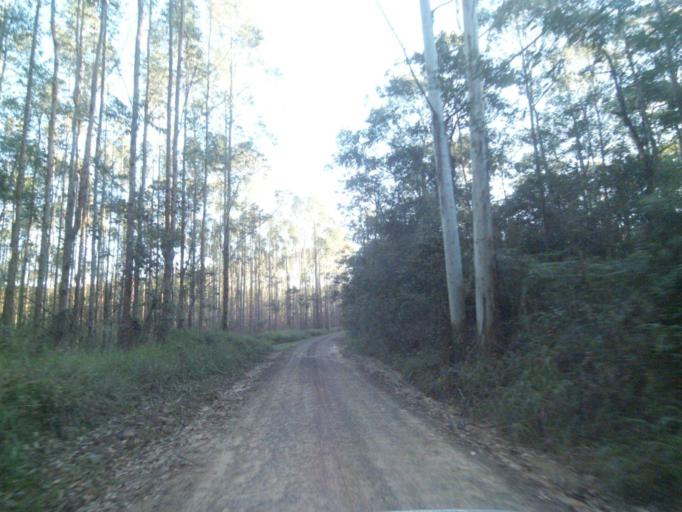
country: BR
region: Parana
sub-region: Telemaco Borba
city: Telemaco Borba
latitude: -24.4944
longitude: -50.5996
